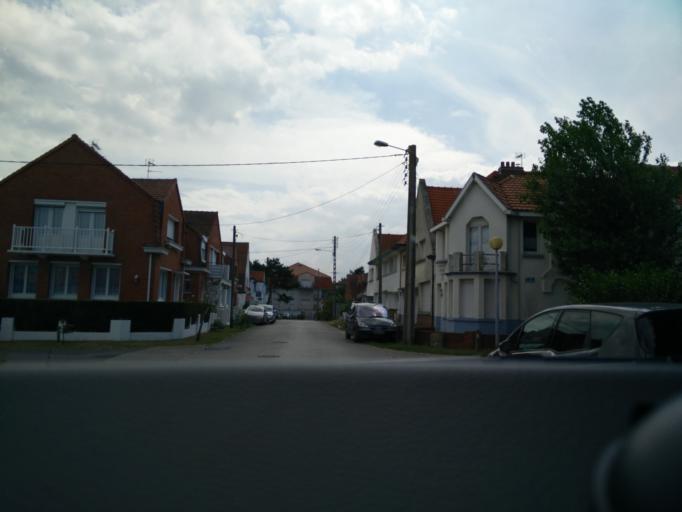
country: FR
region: Nord-Pas-de-Calais
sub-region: Departement du Nord
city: Bray-Dunes
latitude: 51.0777
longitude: 2.5188
